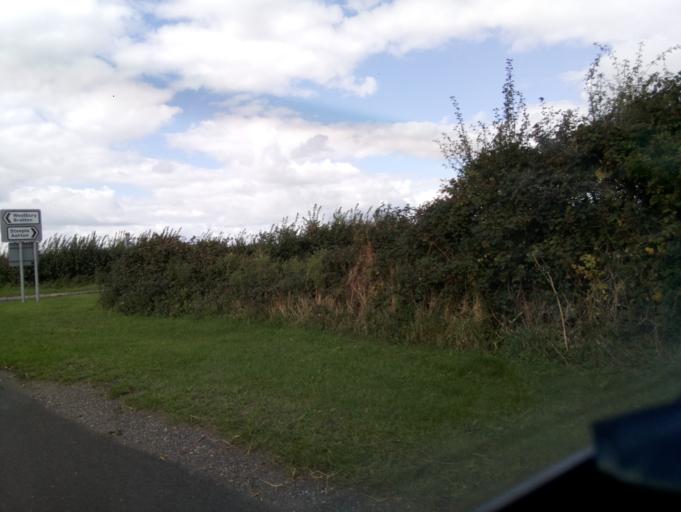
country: GB
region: England
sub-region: Wiltshire
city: Bratton
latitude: 51.2814
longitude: -2.1283
